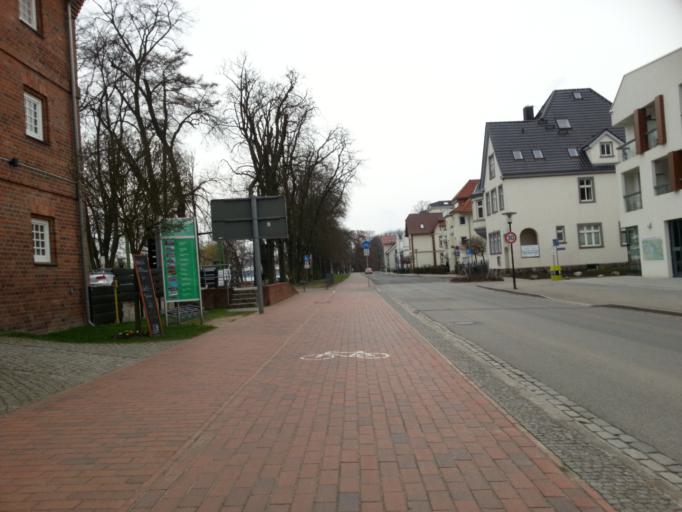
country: DE
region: Mecklenburg-Vorpommern
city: Waren
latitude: 53.5144
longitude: 12.6822
